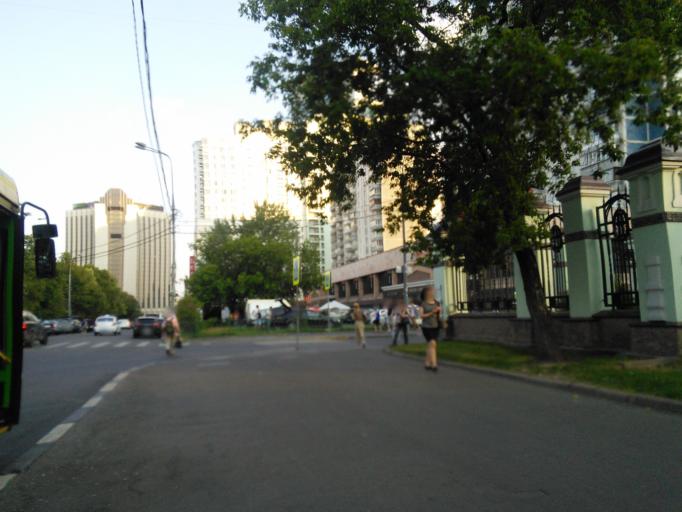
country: RU
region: Moscow
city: Sokol'niki
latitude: 55.7912
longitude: 37.6780
